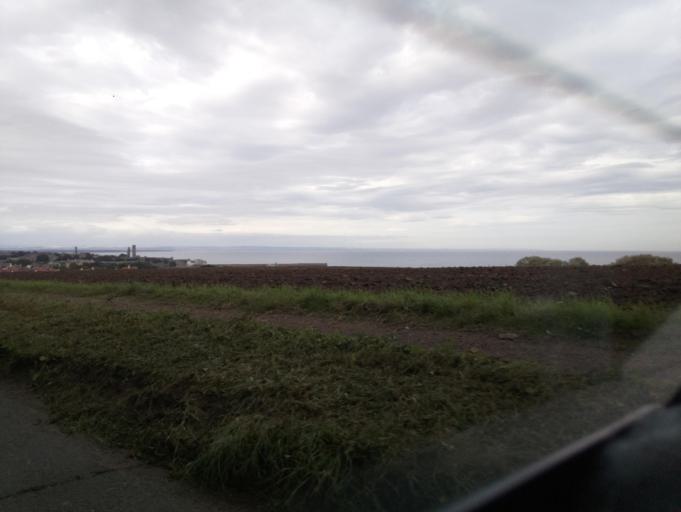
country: GB
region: Scotland
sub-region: Fife
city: Saint Andrews
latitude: 56.3282
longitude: -2.7825
